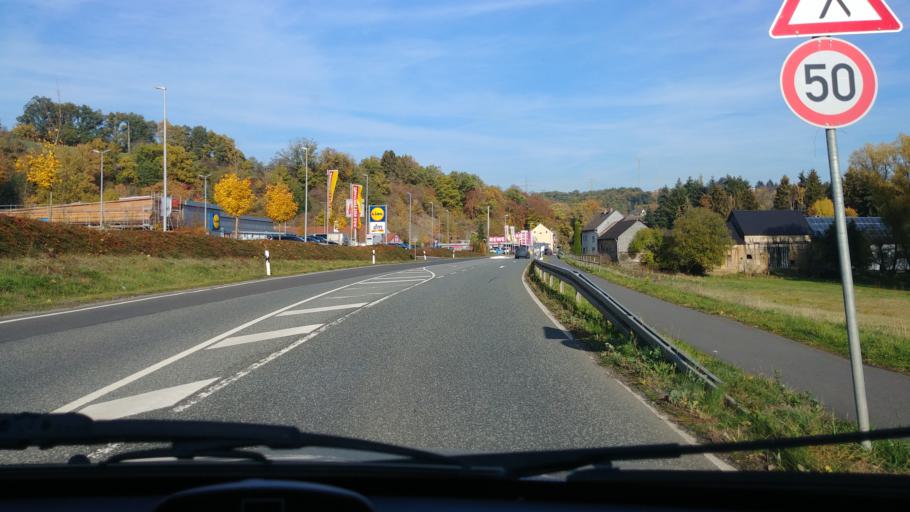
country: DE
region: Rheinland-Pfalz
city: Eisighofen
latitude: 50.2397
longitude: 8.0600
